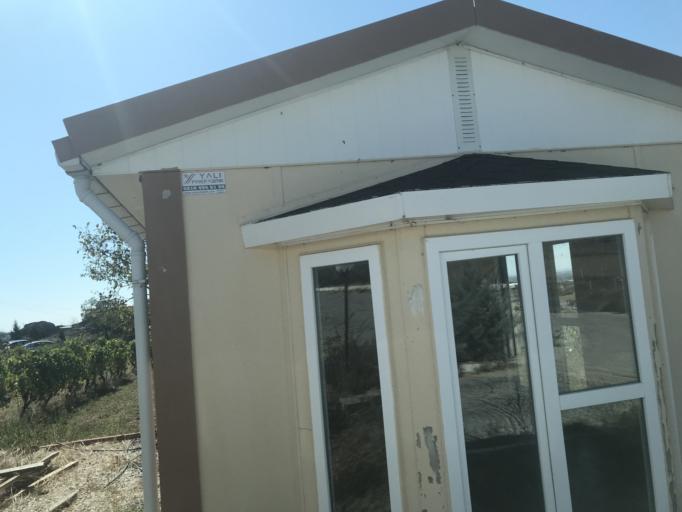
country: TR
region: Kirklareli
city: Kirklareli
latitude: 41.7879
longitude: 27.2342
